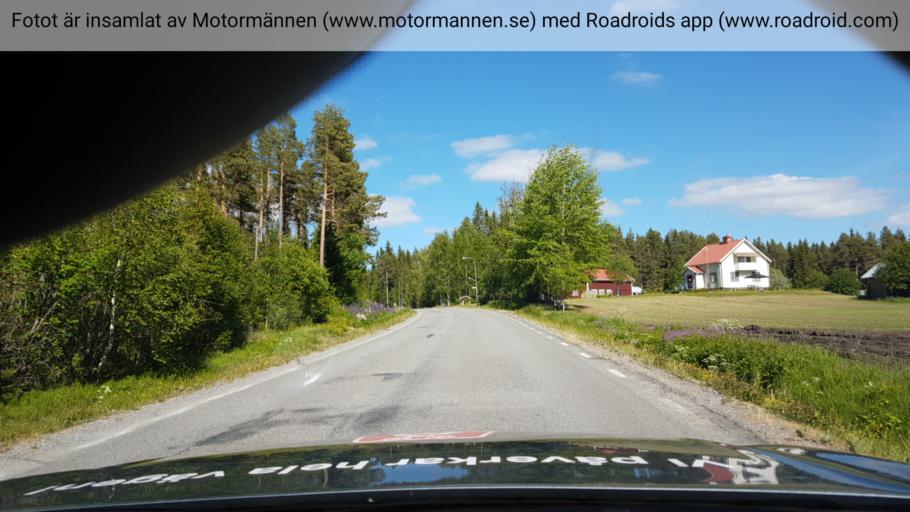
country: SE
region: Jaemtland
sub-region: OEstersunds Kommun
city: Brunflo
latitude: 63.0271
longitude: 14.8747
